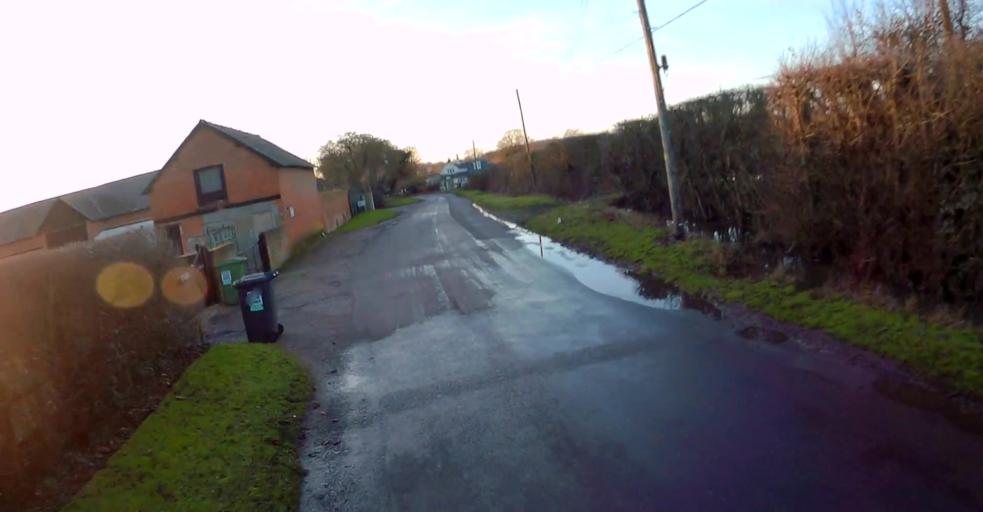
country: GB
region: England
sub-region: West Berkshire
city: Stratfield Mortimer
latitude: 51.3489
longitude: -1.0258
